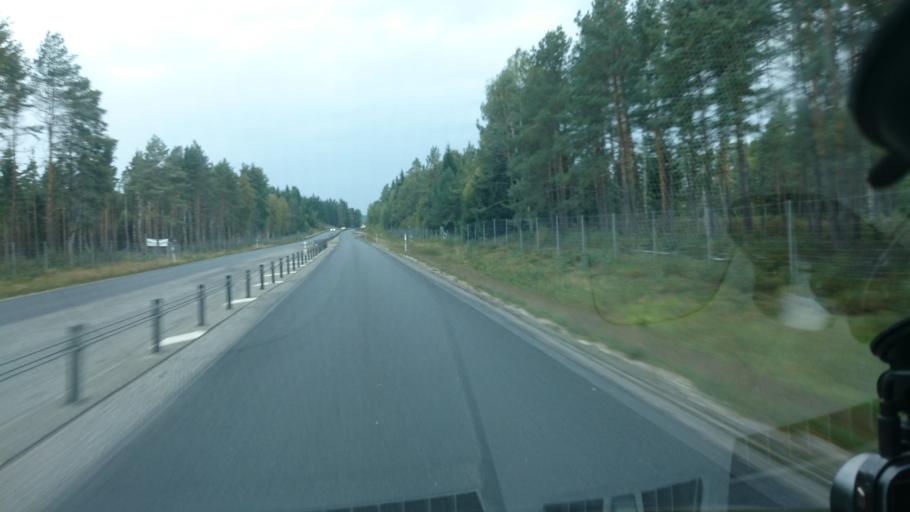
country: SE
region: Vaestra Goetaland
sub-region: Tranemo Kommun
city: Langhem
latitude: 57.6118
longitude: 13.1279
